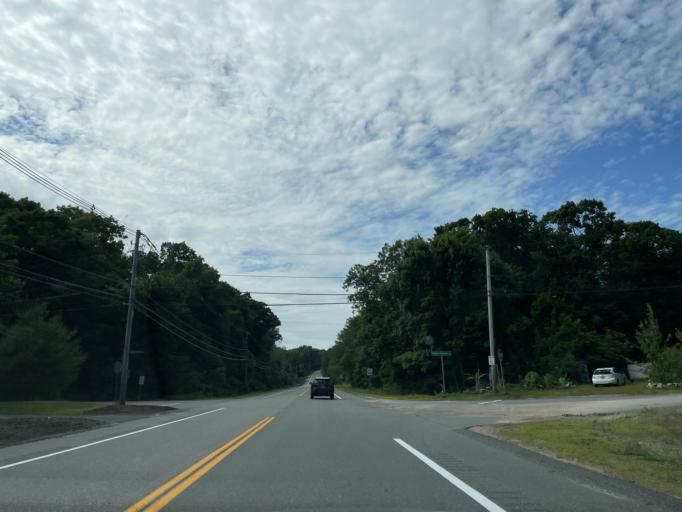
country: US
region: Rhode Island
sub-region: Kent County
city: West Greenwich
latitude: 41.6248
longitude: -71.6786
